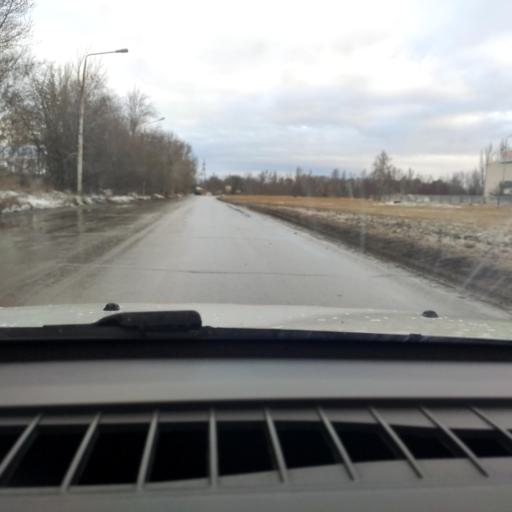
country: RU
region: Samara
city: Podstepki
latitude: 53.5825
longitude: 49.2208
